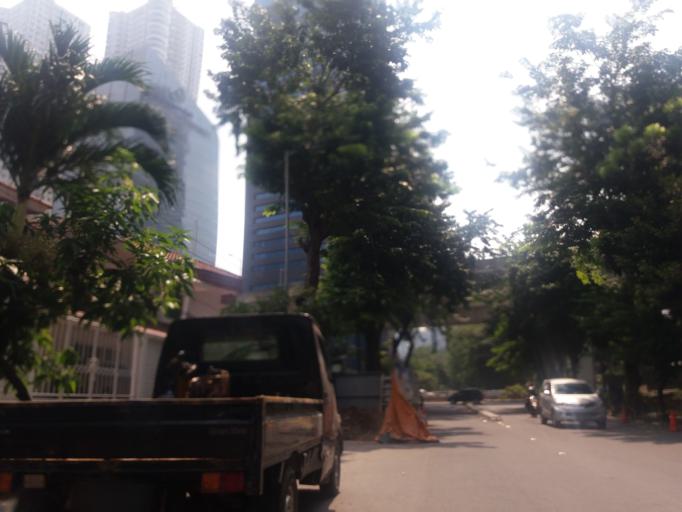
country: ID
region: Jakarta Raya
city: Jakarta
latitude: -6.2266
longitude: 106.8319
